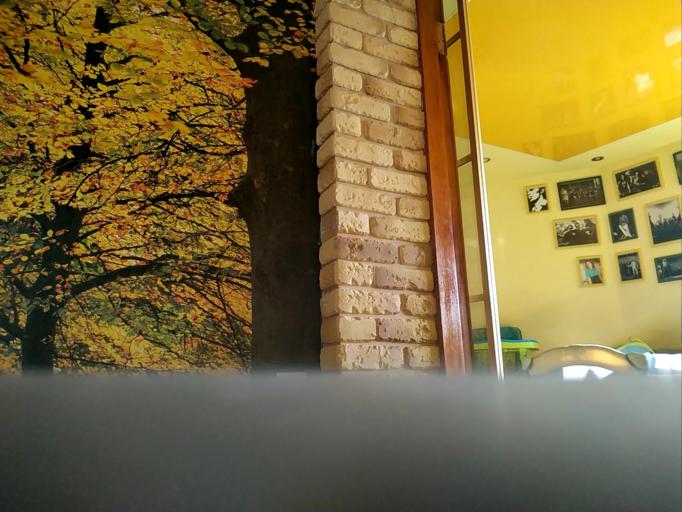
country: RU
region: Kaluga
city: Mosal'sk
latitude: 54.5491
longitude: 35.1089
